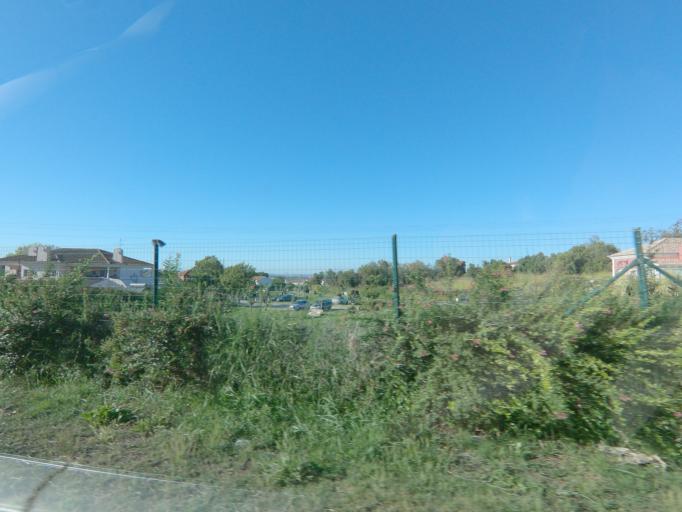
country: PT
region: Setubal
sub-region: Palmela
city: Palmela
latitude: 38.5677
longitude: -8.9200
